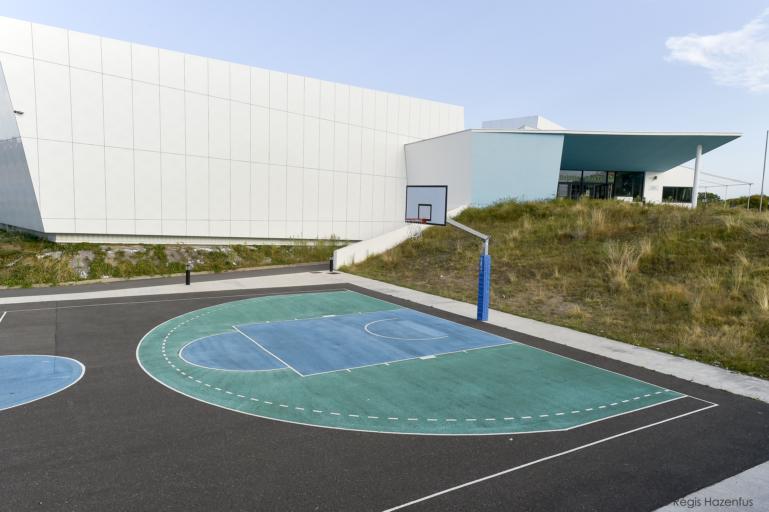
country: FR
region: Aquitaine
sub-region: Departement de la Gironde
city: Talence
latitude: 44.7967
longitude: -0.5772
